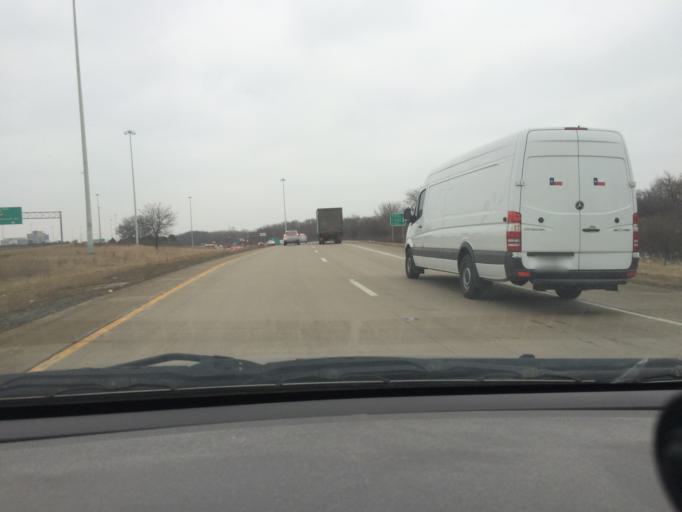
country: US
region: Illinois
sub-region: Cook County
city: Hoffman Estates
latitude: 42.0333
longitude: -88.0305
